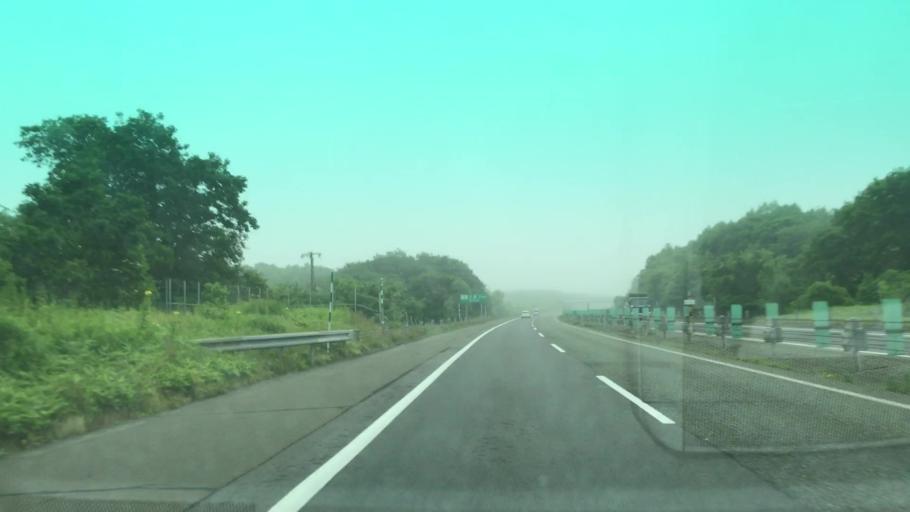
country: JP
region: Hokkaido
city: Chitose
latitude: 42.8310
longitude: 141.6117
